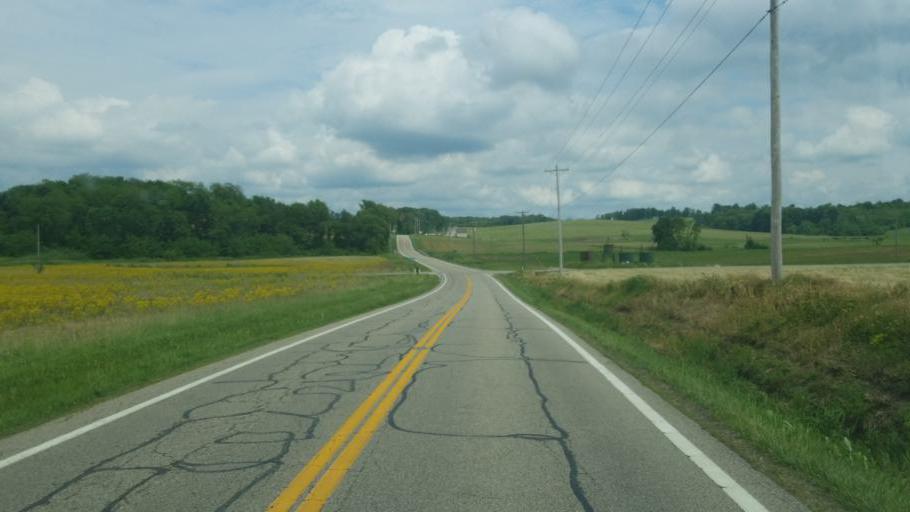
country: US
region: Ohio
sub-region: Perry County
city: Thornport
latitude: 39.9069
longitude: -82.3722
